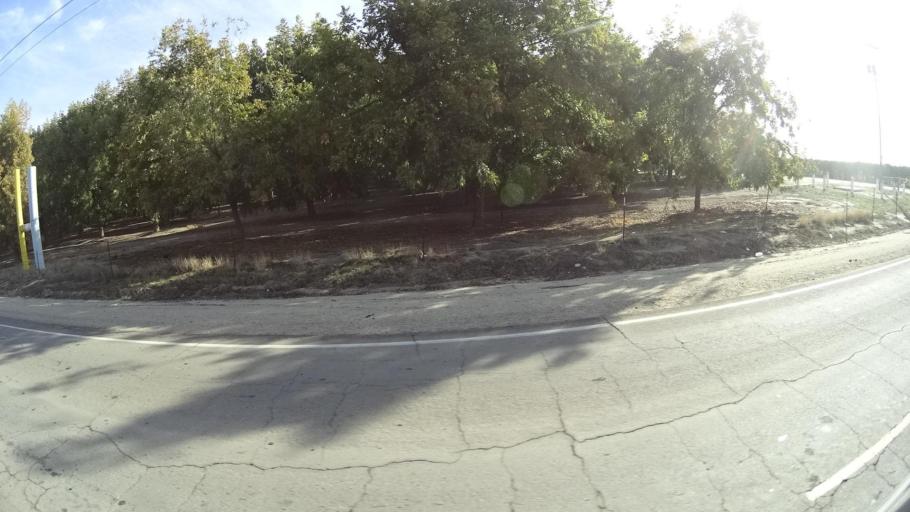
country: US
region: California
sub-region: Kern County
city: McFarland
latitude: 35.6170
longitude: -119.2044
